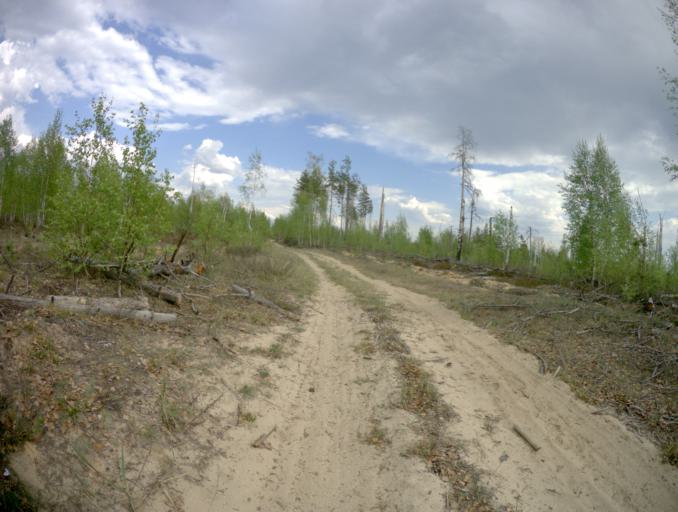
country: RU
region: Ivanovo
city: Talitsy
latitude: 56.4452
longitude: 42.2528
